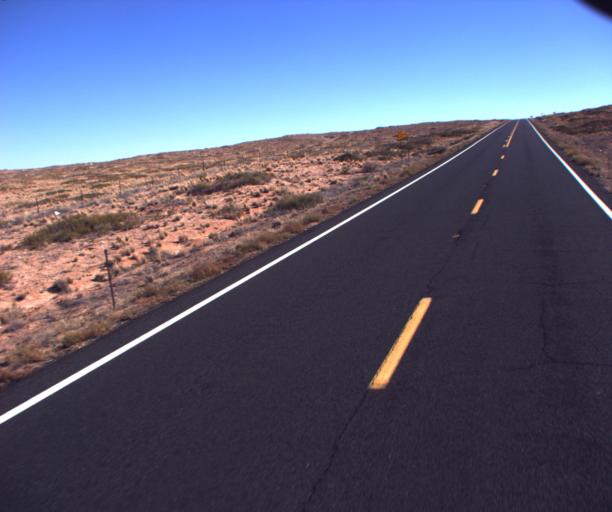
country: US
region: Arizona
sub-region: Coconino County
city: Tuba City
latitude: 36.0202
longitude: -111.1256
